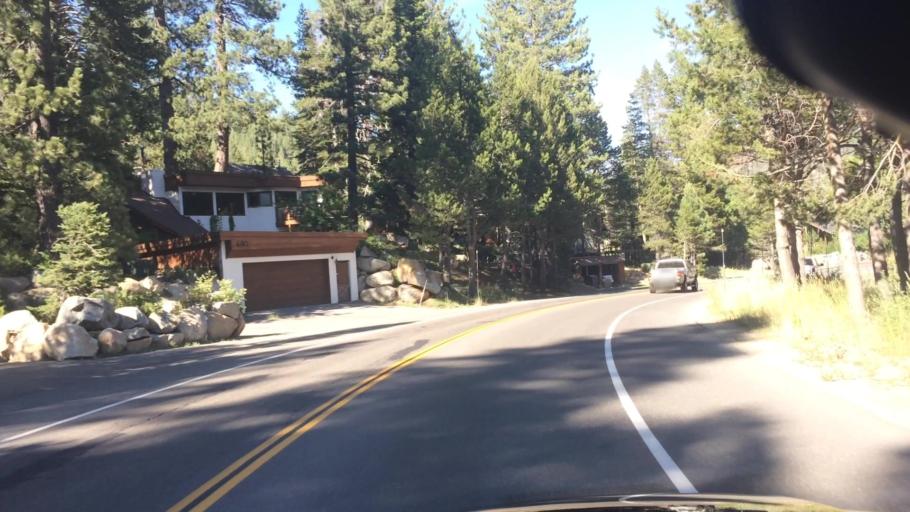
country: US
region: California
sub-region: Placer County
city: Sunnyside-Tahoe City
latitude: 39.2069
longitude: -120.2149
